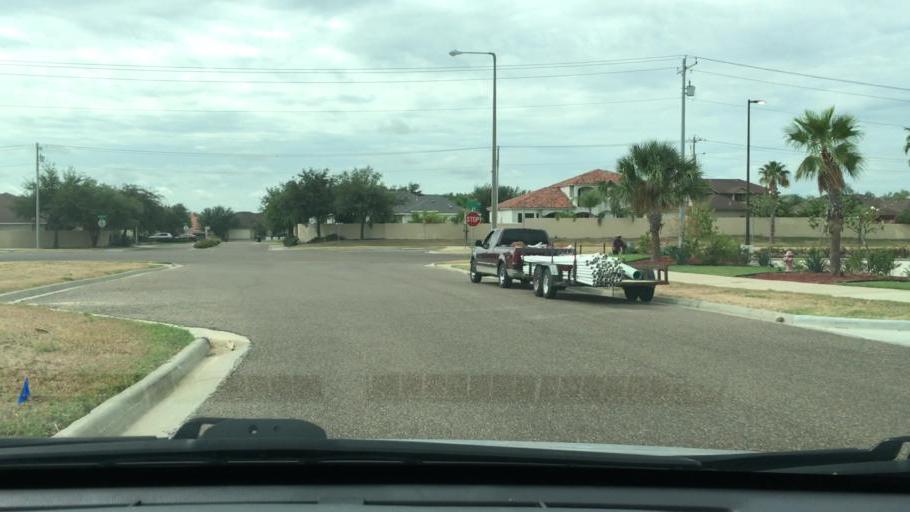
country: US
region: Texas
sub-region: Webb County
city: Laredo
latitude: 27.6038
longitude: -99.4831
